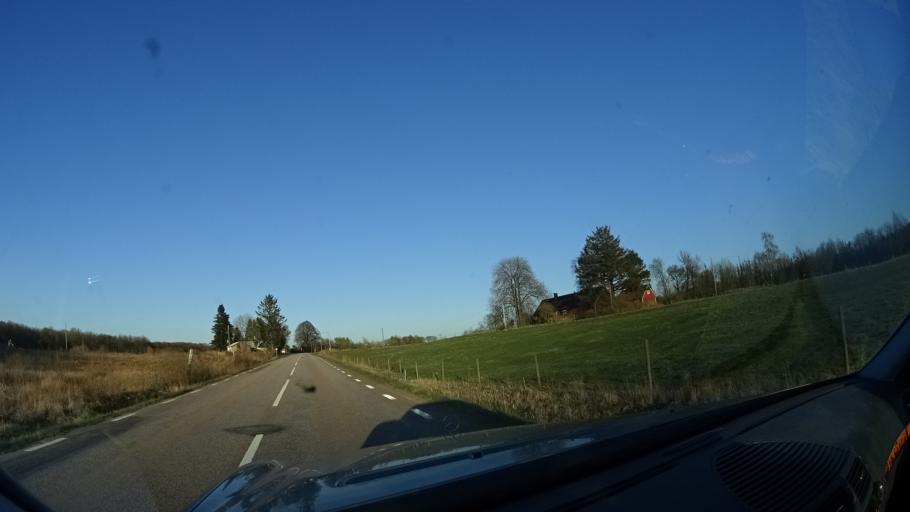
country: SE
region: Skane
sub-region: Svalovs Kommun
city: Kagerod
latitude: 55.9794
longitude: 13.1847
